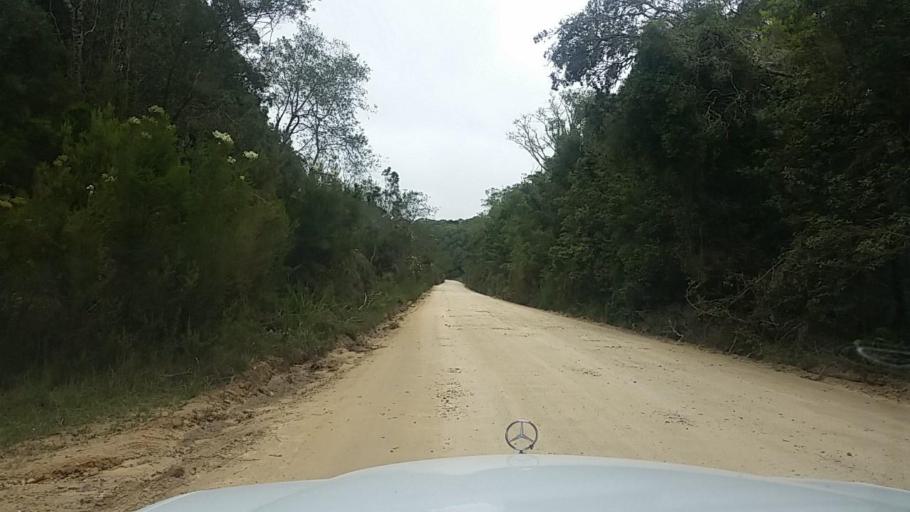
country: ZA
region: Western Cape
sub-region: Eden District Municipality
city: Knysna
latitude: -33.9654
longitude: 23.1516
